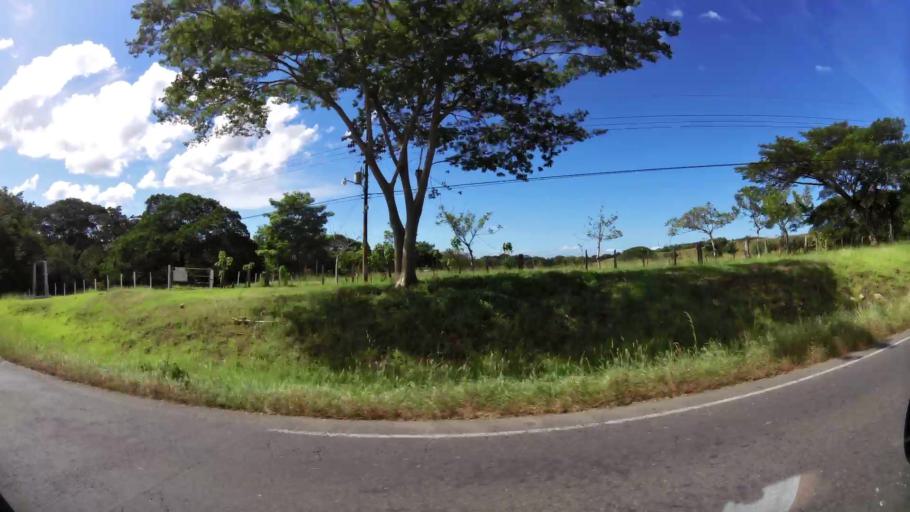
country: CR
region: Guanacaste
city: Juntas
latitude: 10.3224
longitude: -85.0475
